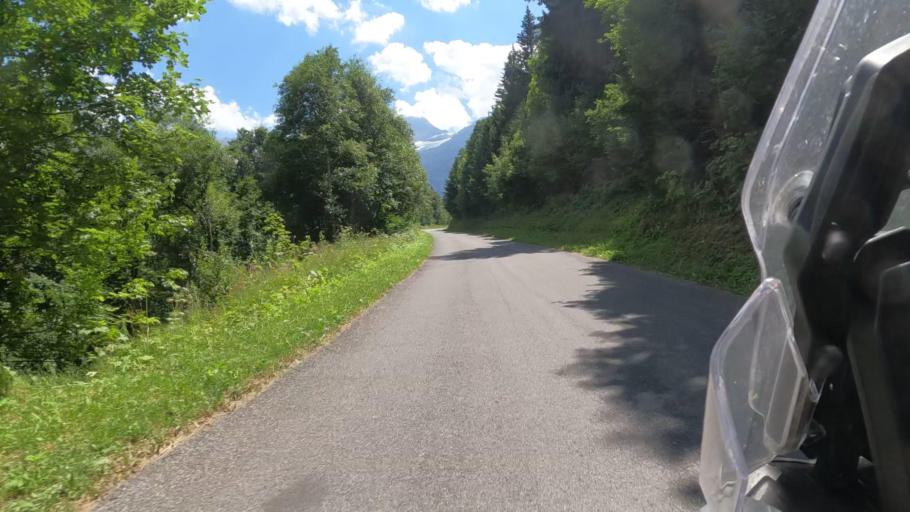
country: CH
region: Vaud
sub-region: Aigle District
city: Villars-sur-Ollon
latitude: 46.3449
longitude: 7.1465
